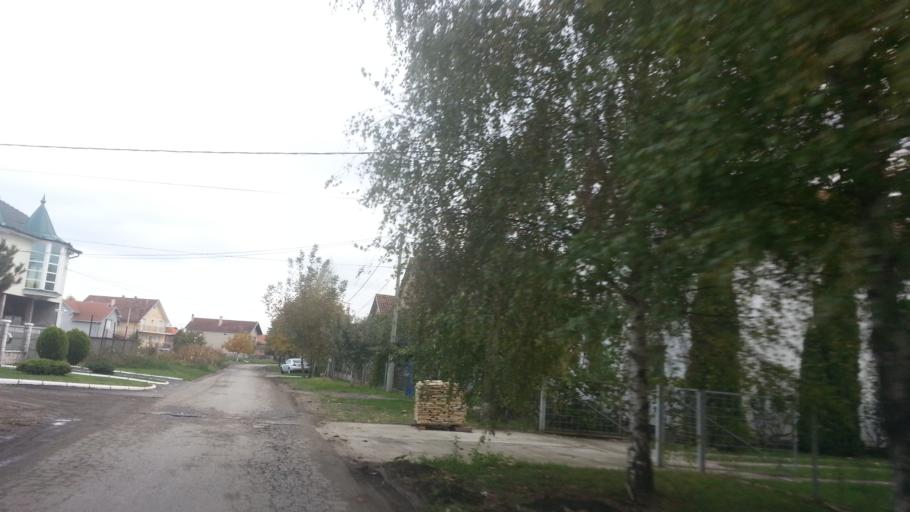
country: RS
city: Novi Banovci
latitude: 44.9168
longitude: 20.2753
